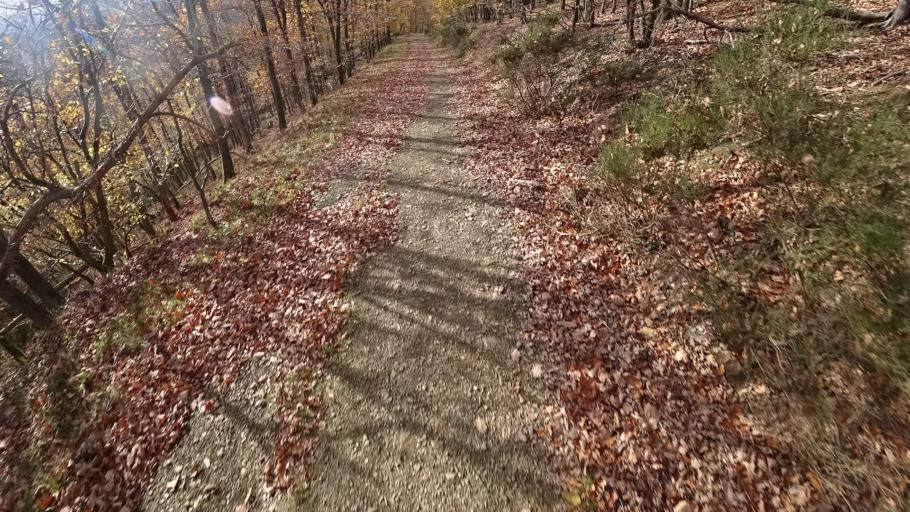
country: DE
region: Rheinland-Pfalz
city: Lind
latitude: 50.4888
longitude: 6.9221
